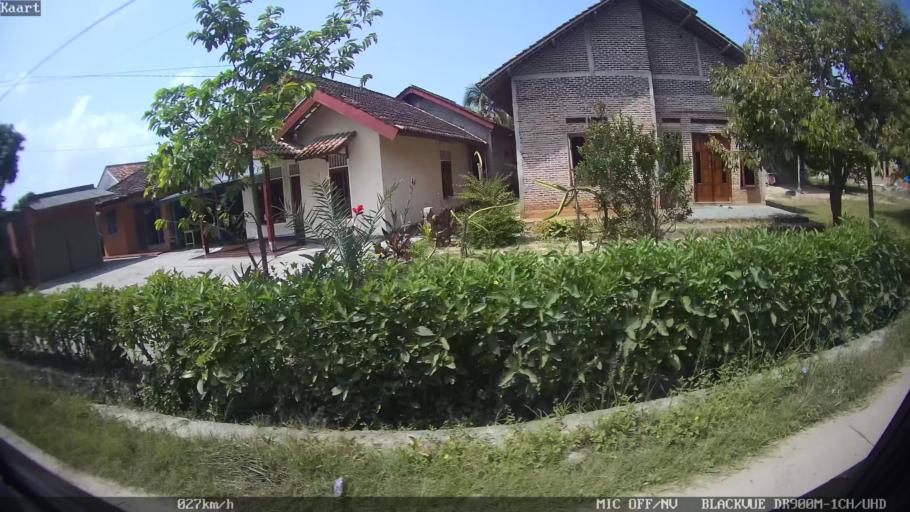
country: ID
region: Lampung
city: Natar
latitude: -5.2663
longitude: 105.1902
